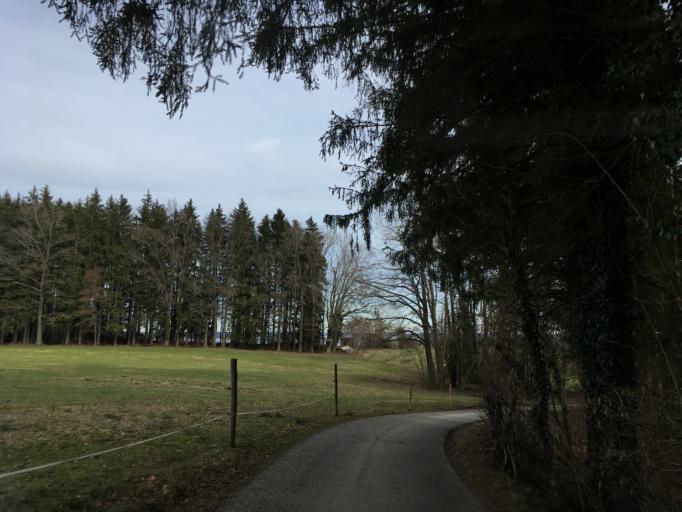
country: DE
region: Bavaria
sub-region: Upper Bavaria
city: Bernau am Chiemsee
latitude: 47.8214
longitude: 12.3522
